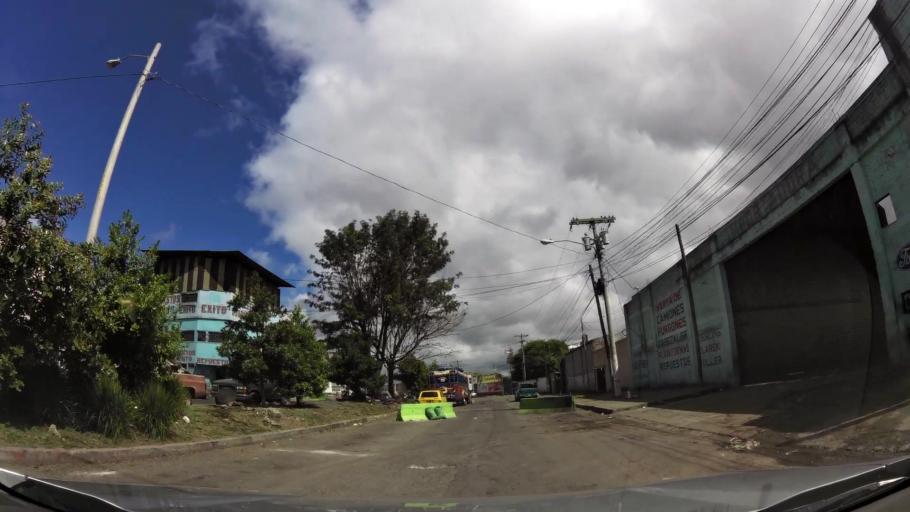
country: GT
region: Guatemala
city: Guatemala City
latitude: 14.6122
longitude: -90.5257
